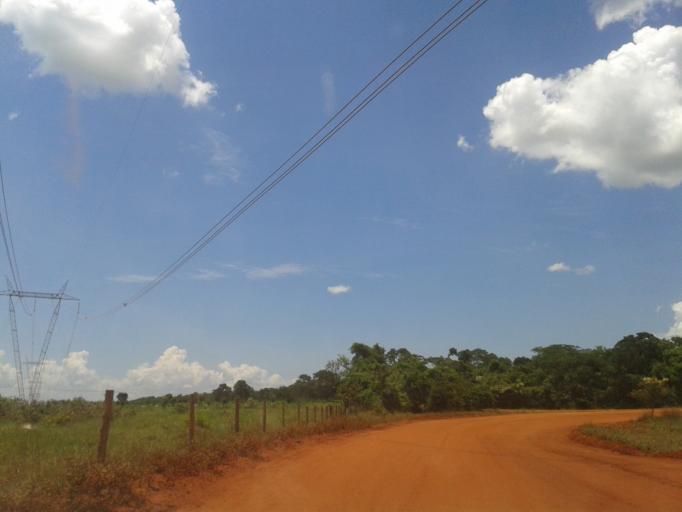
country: BR
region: Minas Gerais
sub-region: Santa Vitoria
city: Santa Vitoria
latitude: -19.1616
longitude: -50.4077
